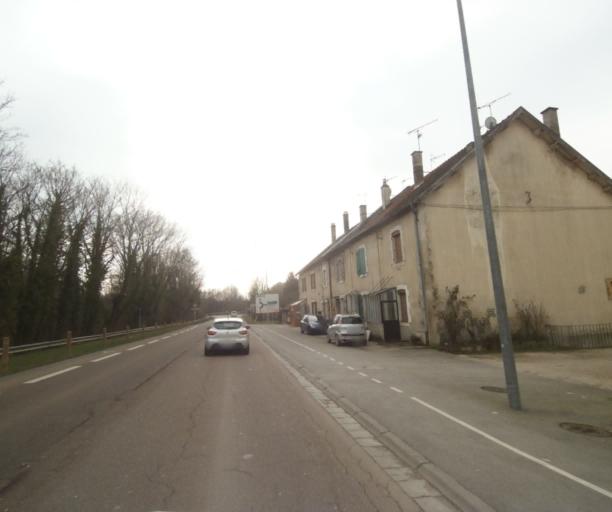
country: FR
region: Lorraine
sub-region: Departement de la Meuse
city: Ancerville
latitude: 48.6244
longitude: 4.9920
